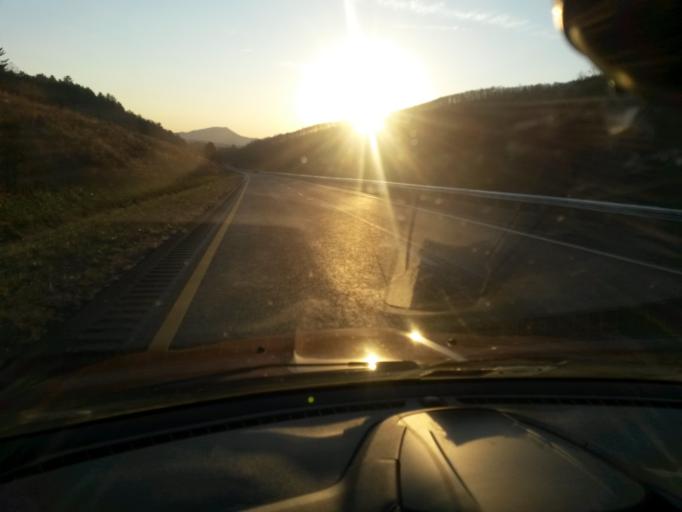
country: US
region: Virginia
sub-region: Alleghany County
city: Clifton Forge
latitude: 37.8349
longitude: -79.6495
